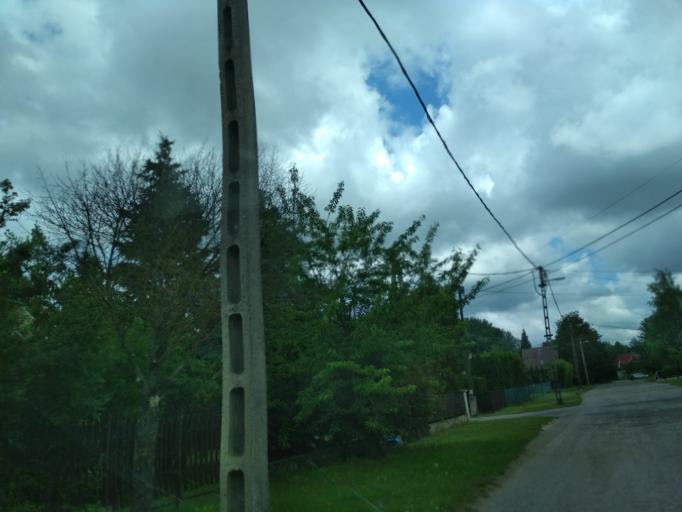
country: HU
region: Jasz-Nagykun-Szolnok
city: Tiszafured
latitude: 47.6176
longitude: 20.7366
